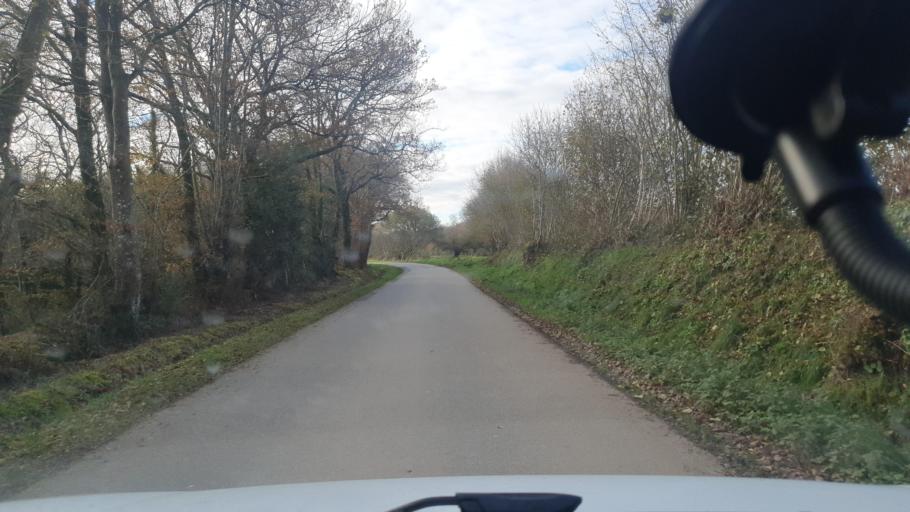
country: FR
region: Brittany
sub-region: Departement du Finistere
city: Briec
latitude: 48.1189
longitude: -4.0078
